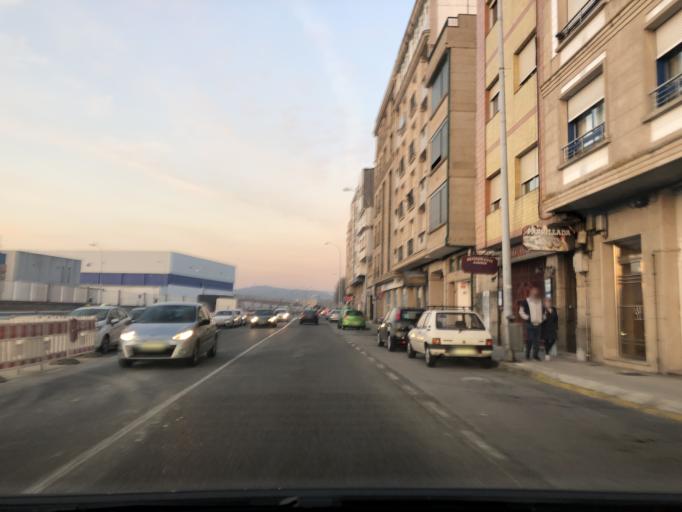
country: ES
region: Galicia
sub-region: Provincia de Pontevedra
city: Marin
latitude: 42.3965
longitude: -8.6924
